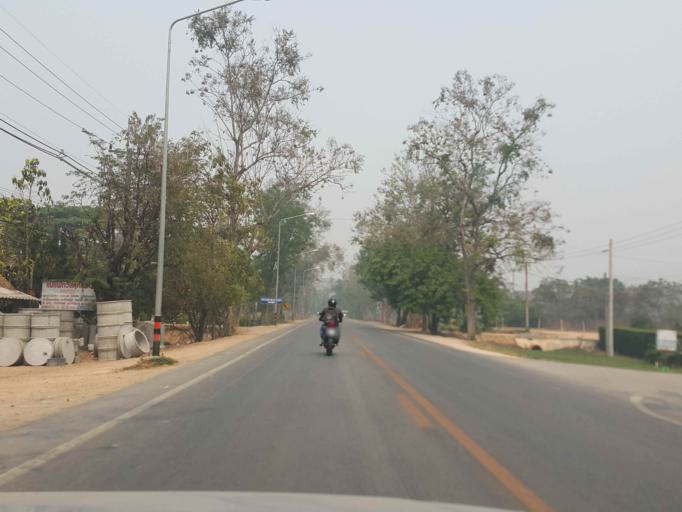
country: TH
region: Chiang Mai
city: Mae Taeng
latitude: 18.9956
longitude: 98.9773
